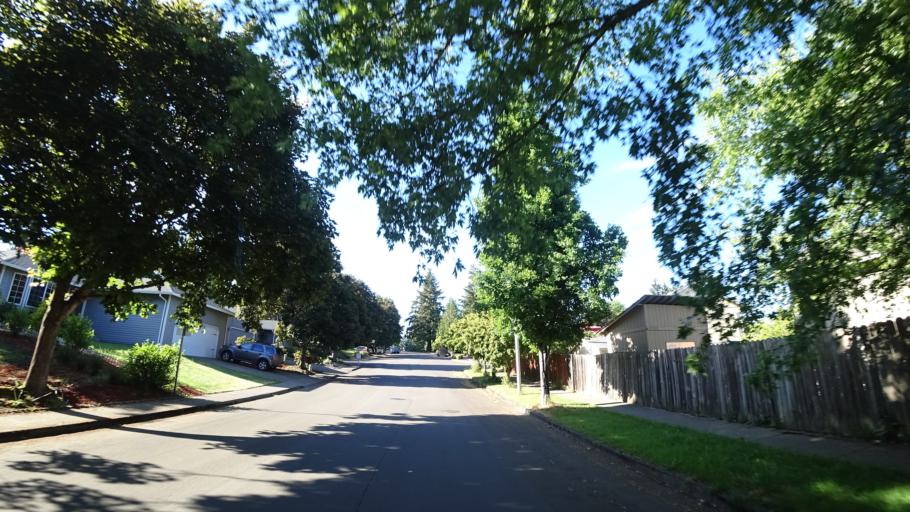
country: US
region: Oregon
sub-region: Washington County
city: Beaverton
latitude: 45.4623
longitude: -122.8118
